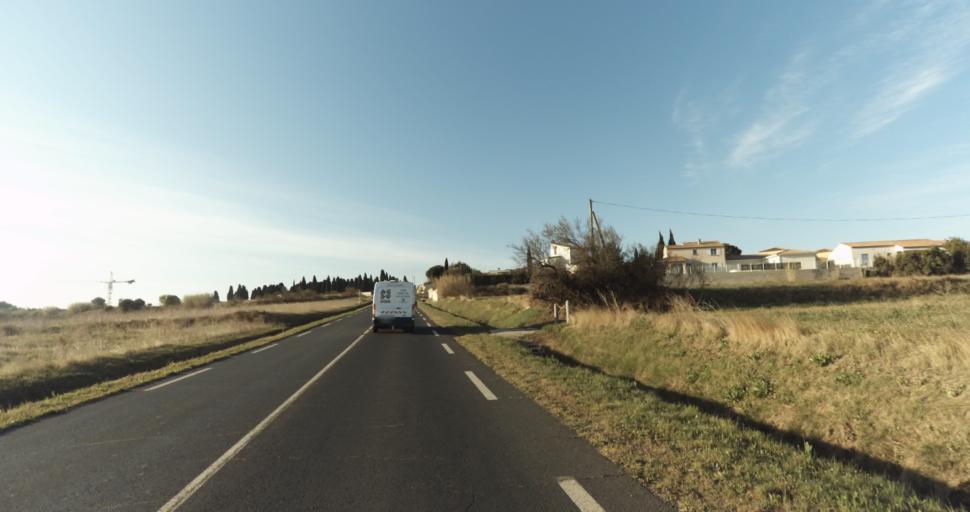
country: FR
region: Languedoc-Roussillon
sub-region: Departement de l'Herault
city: Marseillan
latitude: 43.3630
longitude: 3.5305
